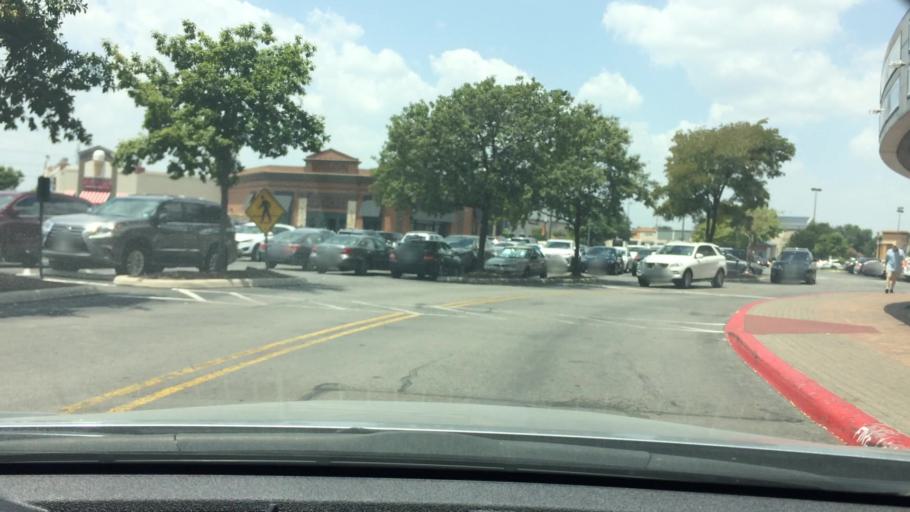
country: US
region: Texas
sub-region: Bexar County
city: Olmos Park
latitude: 29.4951
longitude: -98.4809
